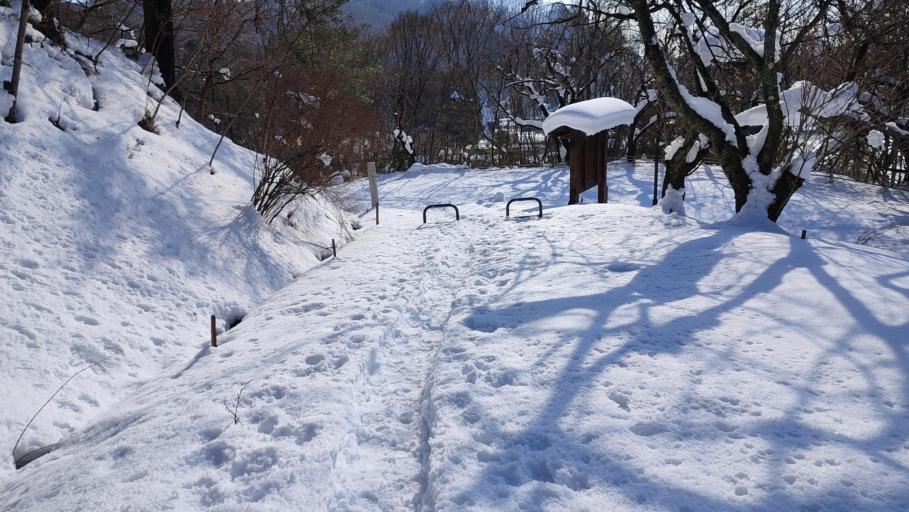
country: JP
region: Akita
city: Kakunodatemachi
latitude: 39.6043
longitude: 140.5623
